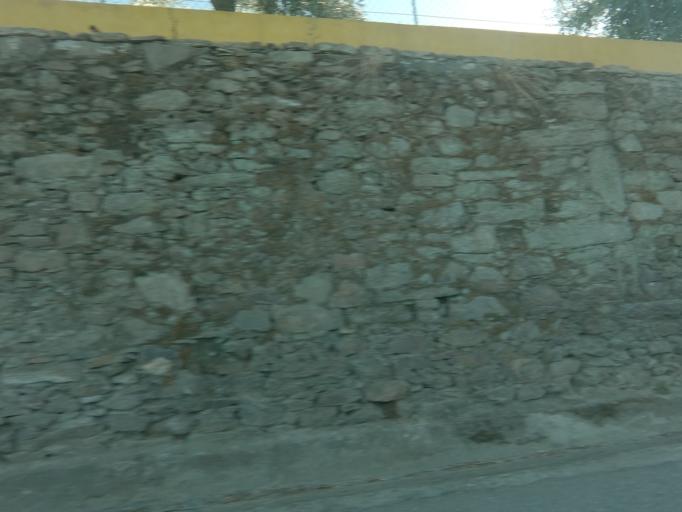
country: PT
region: Vila Real
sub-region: Peso da Regua
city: Godim
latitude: 41.1621
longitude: -7.8122
